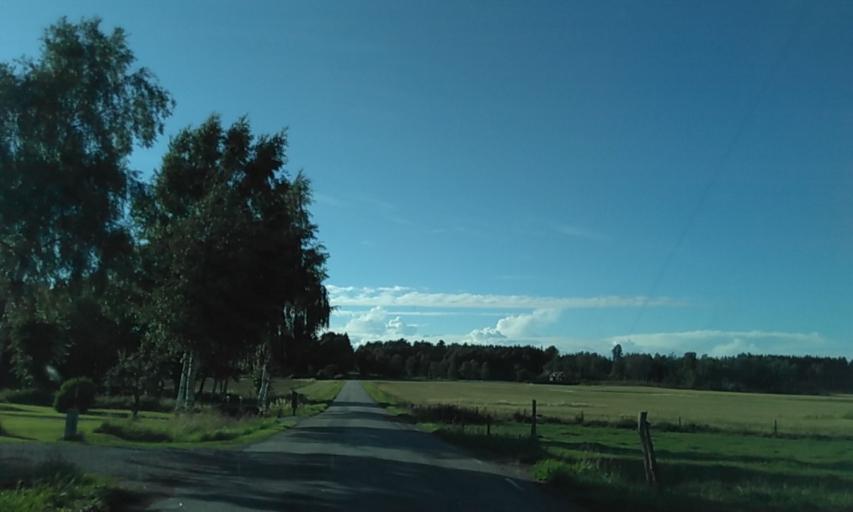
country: SE
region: Vaestra Goetaland
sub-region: Vara Kommun
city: Vara
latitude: 58.3638
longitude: 12.8627
